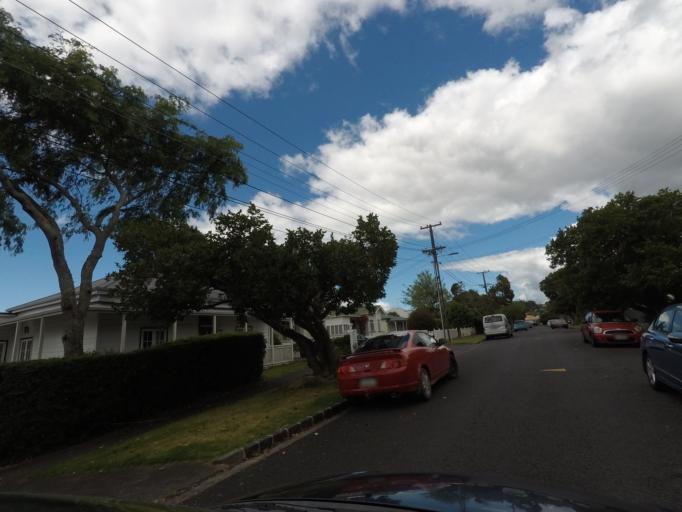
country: NZ
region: Auckland
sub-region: Auckland
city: Auckland
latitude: -36.8797
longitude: 174.7316
